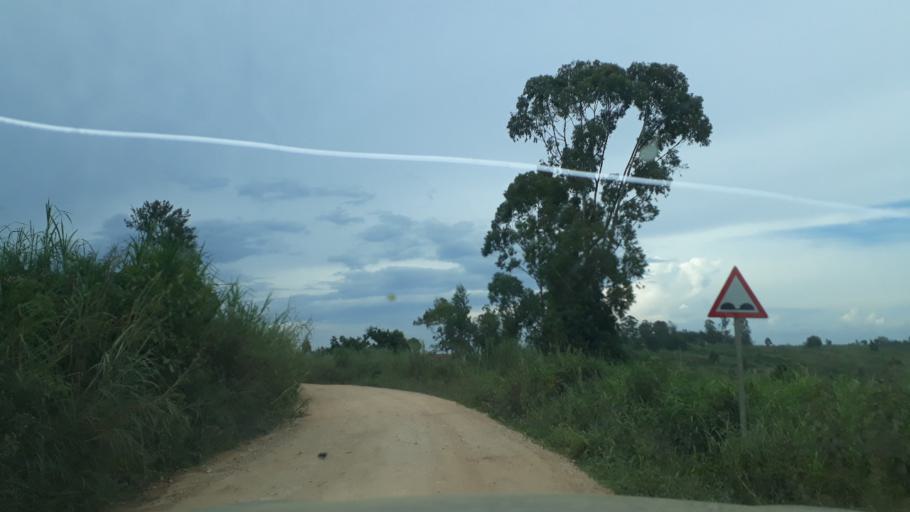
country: CD
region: Eastern Province
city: Bunia
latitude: 1.9158
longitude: 30.5040
